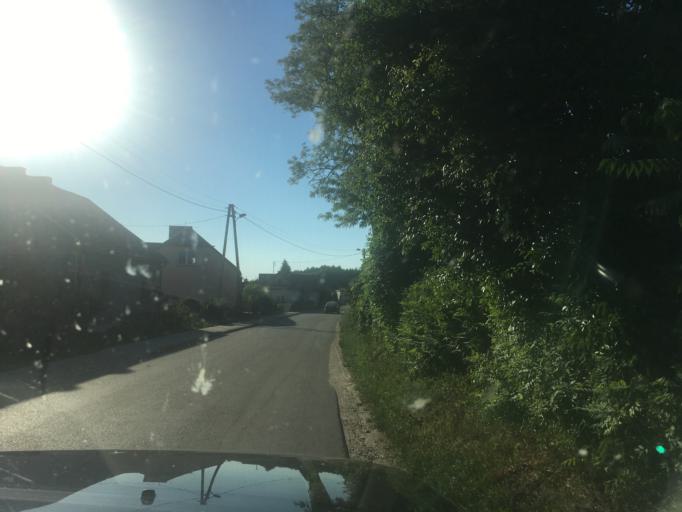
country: PL
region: Warmian-Masurian Voivodeship
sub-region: Powiat ostrodzki
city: Ostroda
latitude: 53.6772
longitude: 20.0456
